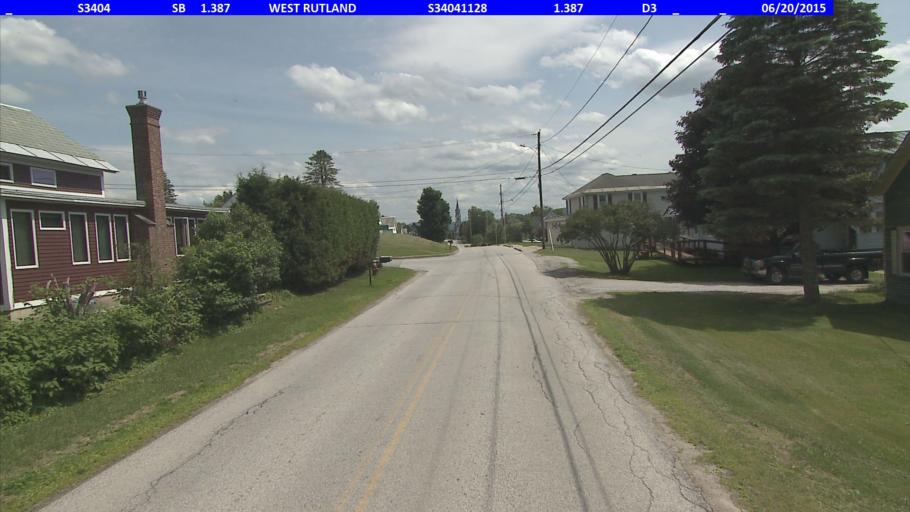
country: US
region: Vermont
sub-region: Rutland County
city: West Rutland
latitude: 43.6112
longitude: -73.0505
